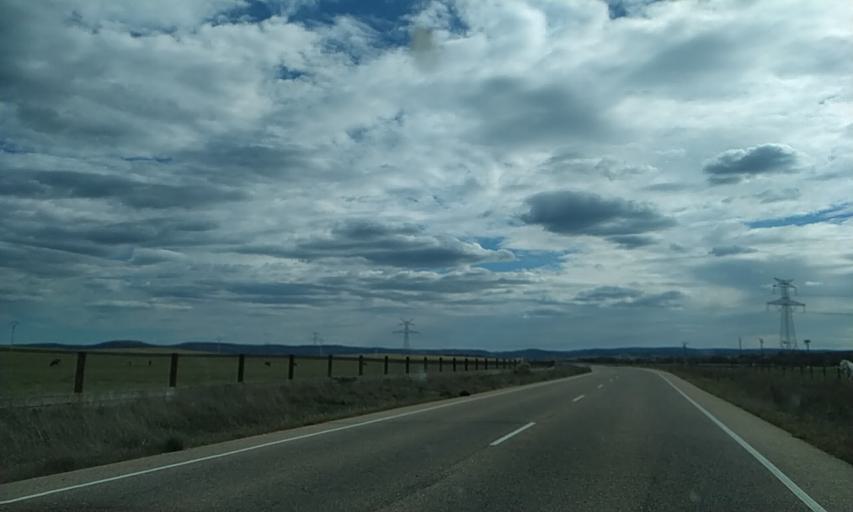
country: ES
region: Castille and Leon
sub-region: Provincia de Salamanca
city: Ciudad Rodrigo
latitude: 40.5530
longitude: -6.5575
